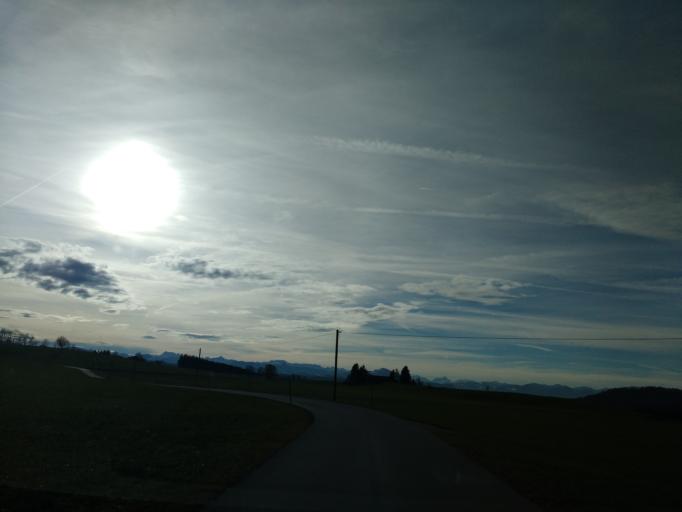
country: DE
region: Bavaria
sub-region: Swabia
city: Wildpoldsried
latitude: 47.7944
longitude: 10.4099
